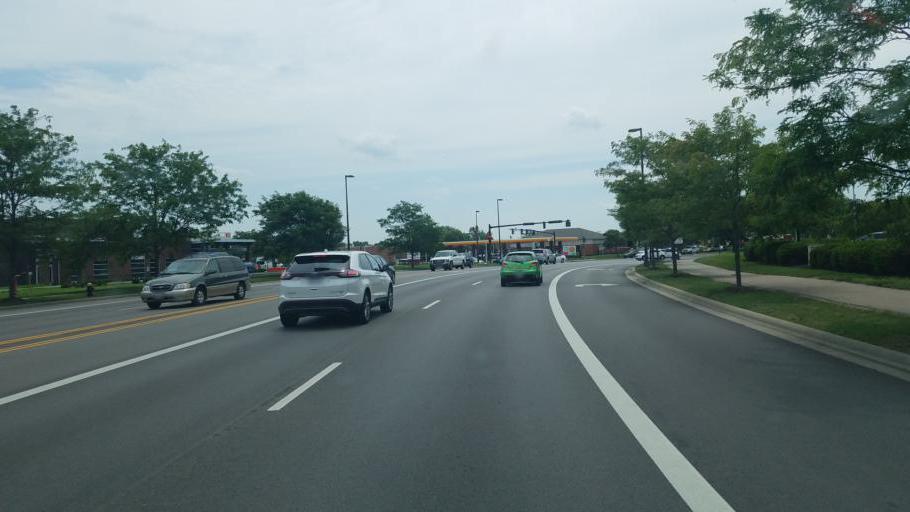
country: US
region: Ohio
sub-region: Franklin County
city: Hilliard
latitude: 40.0329
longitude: -83.1169
